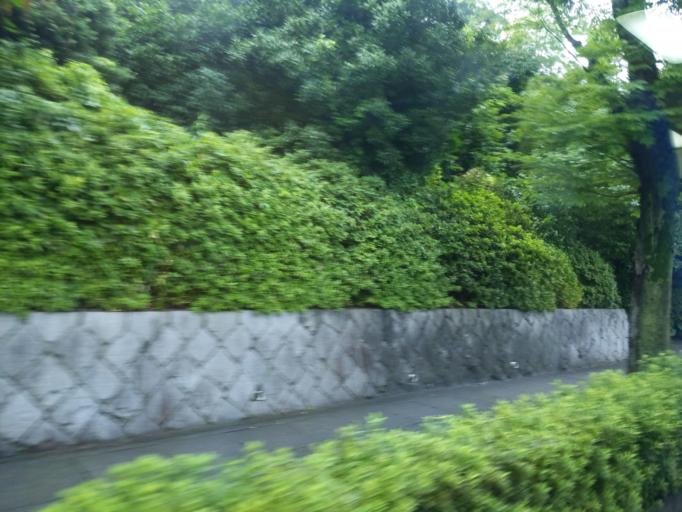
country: JP
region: Tokyo
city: Chofugaoka
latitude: 35.6055
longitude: 139.5659
